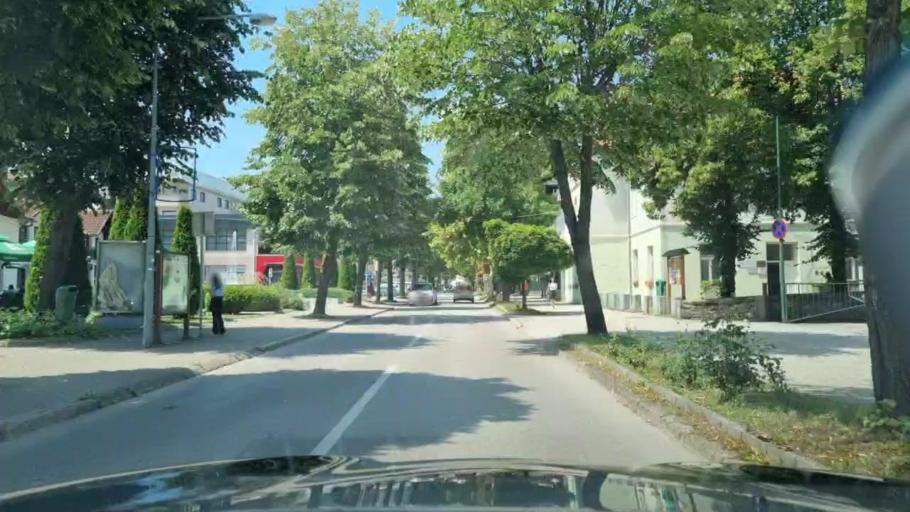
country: BA
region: Federation of Bosnia and Herzegovina
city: Kljuc
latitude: 44.5325
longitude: 16.7776
